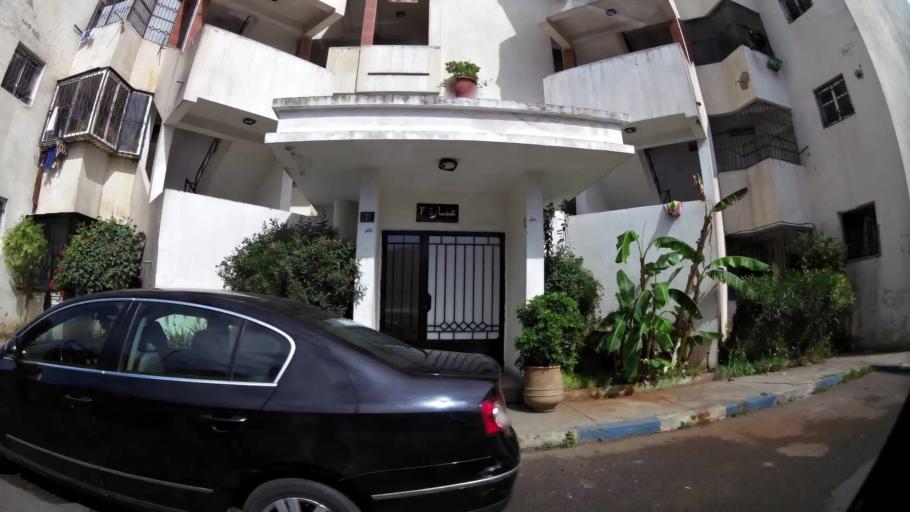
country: MA
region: Grand Casablanca
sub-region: Casablanca
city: Casablanca
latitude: 33.5778
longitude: -7.5851
